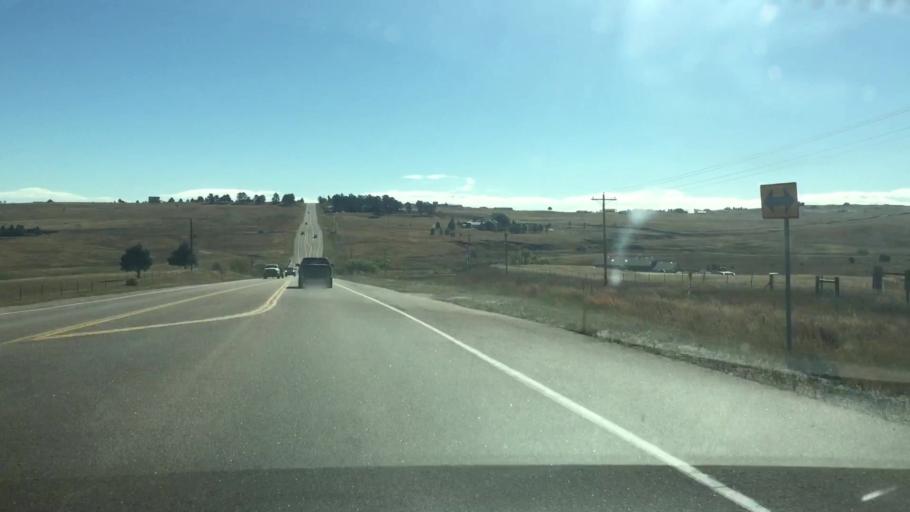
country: US
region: Colorado
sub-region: Elbert County
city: Elizabeth
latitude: 39.3597
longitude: -104.5384
